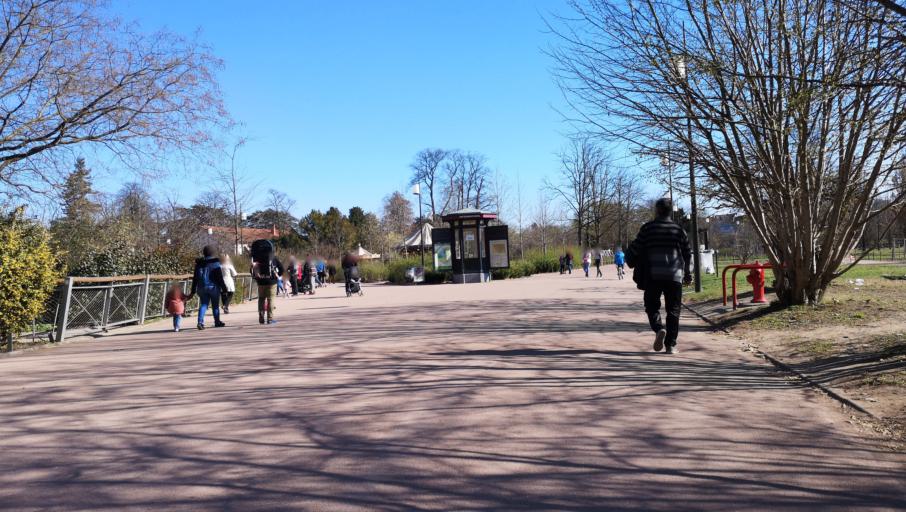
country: FR
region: Rhone-Alpes
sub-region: Departement du Rhone
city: Caluire-et-Cuire
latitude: 45.7775
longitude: 4.8526
